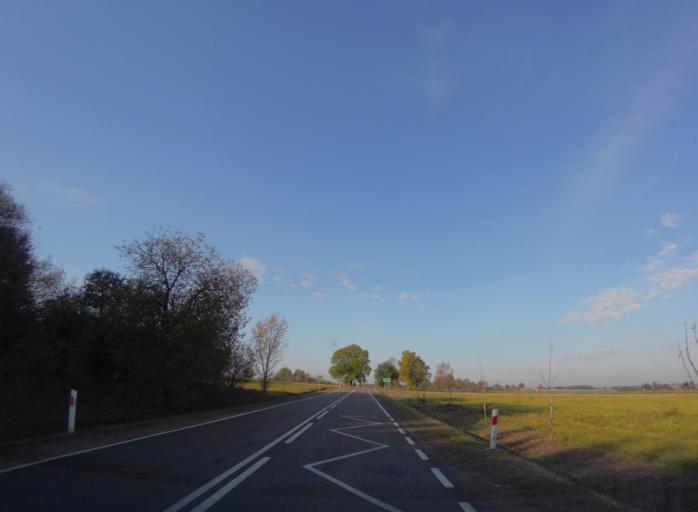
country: PL
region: Masovian Voivodeship
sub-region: Powiat siedlecki
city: Mordy
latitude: 52.2171
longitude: 22.5633
